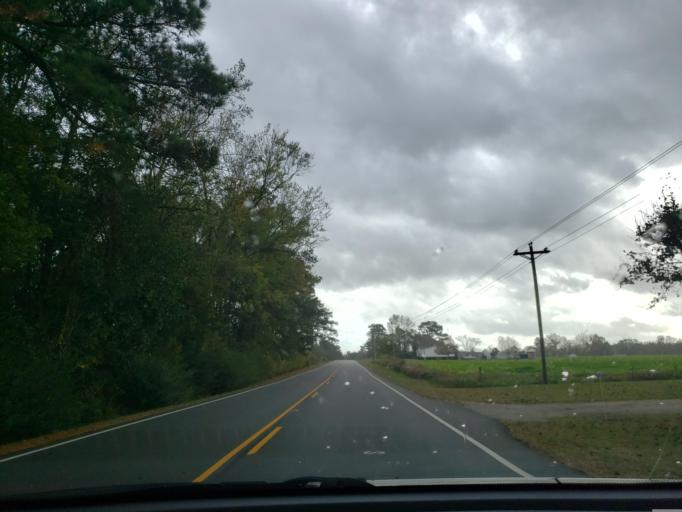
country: US
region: North Carolina
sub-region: Duplin County
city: Beulaville
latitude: 34.8542
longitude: -77.8734
